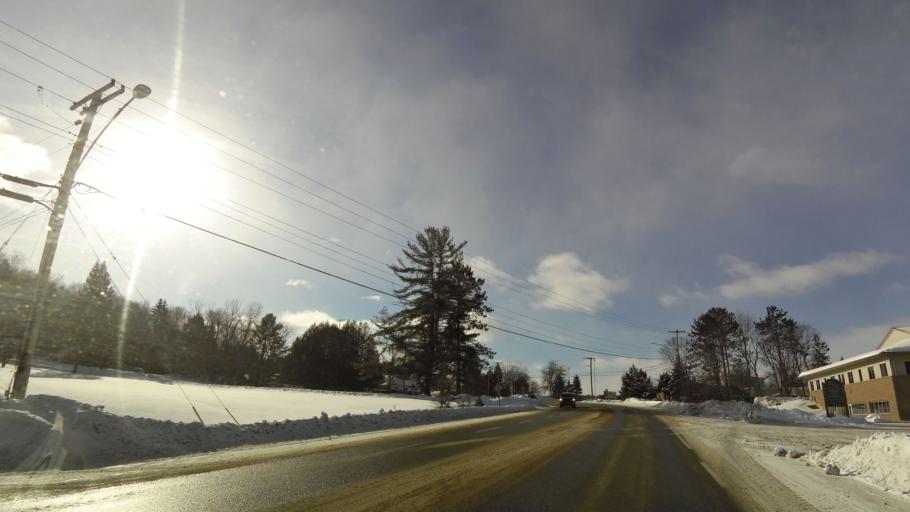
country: CA
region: Ontario
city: Bancroft
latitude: 45.0390
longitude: -78.5272
